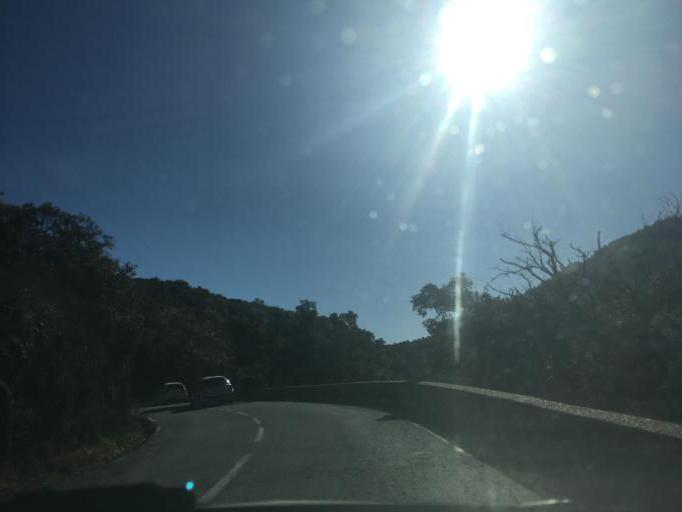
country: FR
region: Provence-Alpes-Cote d'Azur
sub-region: Departement du Var
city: La Garde-Freinet
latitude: 43.3296
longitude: 6.4605
